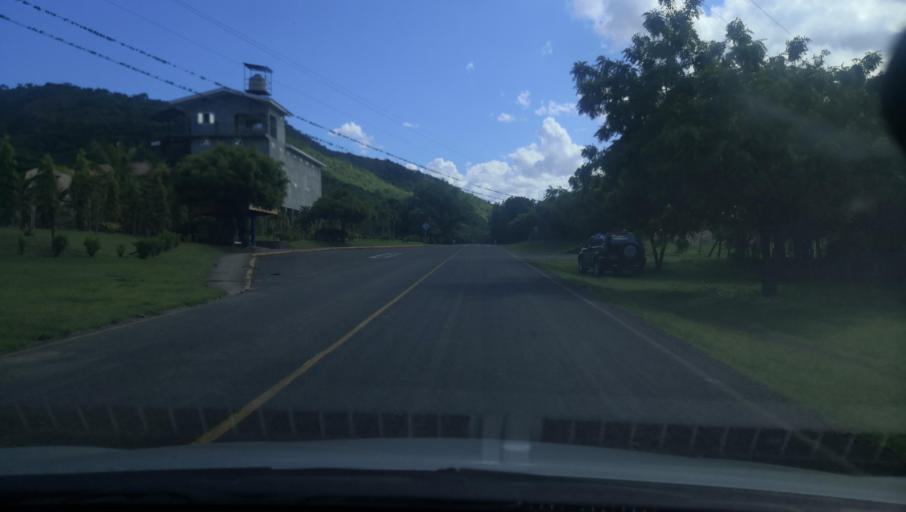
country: NI
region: Madriz
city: Somoto
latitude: 13.4669
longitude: -86.6343
